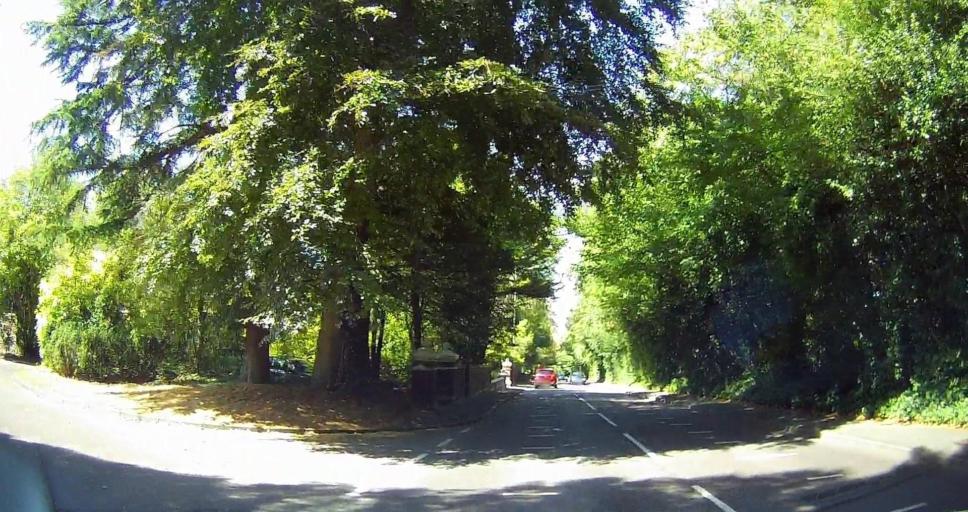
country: GB
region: England
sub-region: Staffordshire
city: Codsall
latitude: 52.6023
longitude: -2.1764
